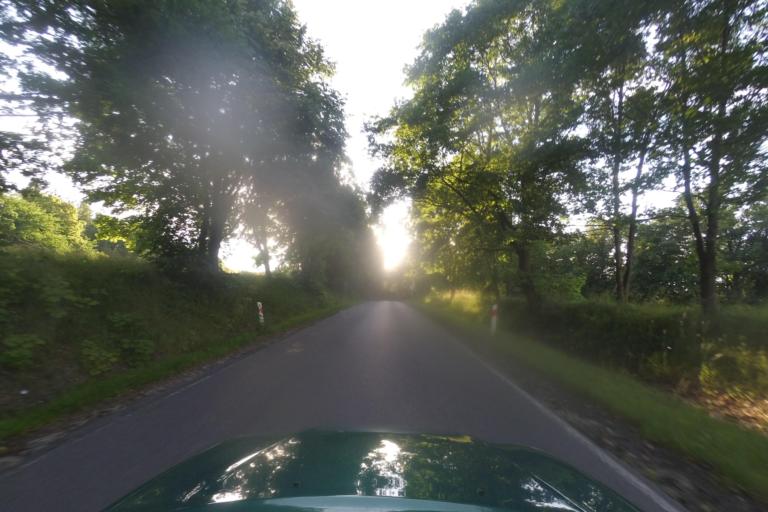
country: PL
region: Lower Silesian Voivodeship
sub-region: Powiat dzierzoniowski
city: Niemcza
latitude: 50.7175
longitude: 16.7979
